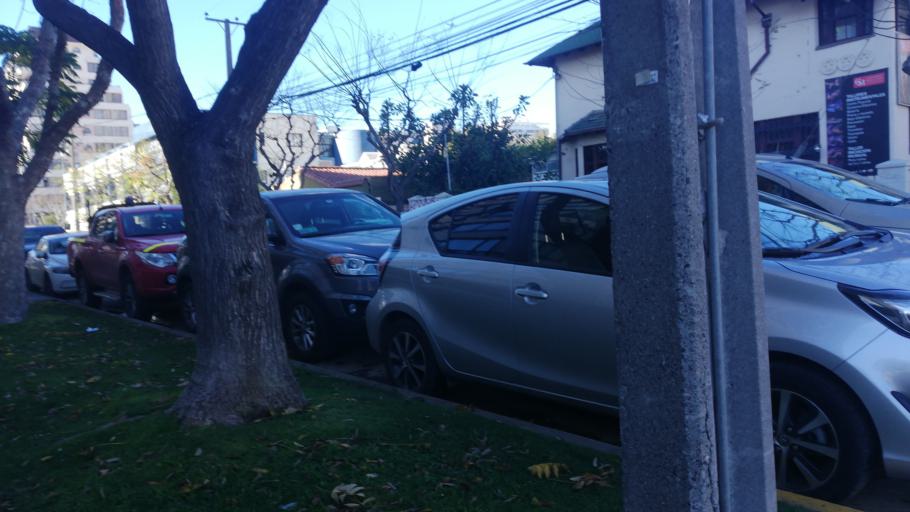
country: CL
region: Valparaiso
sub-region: Provincia de Valparaiso
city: Vina del Mar
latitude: -33.0166
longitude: -71.5489
